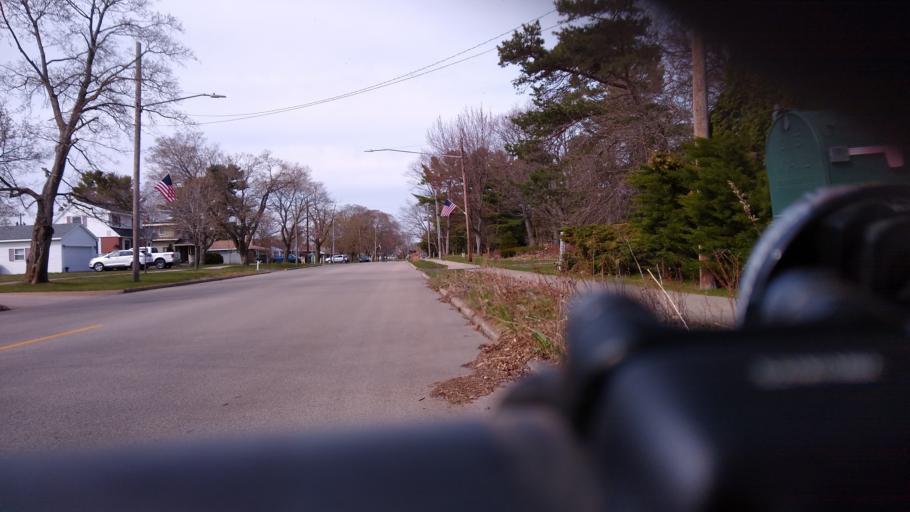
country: US
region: Michigan
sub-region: Delta County
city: Escanaba
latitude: 45.7262
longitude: -87.0668
